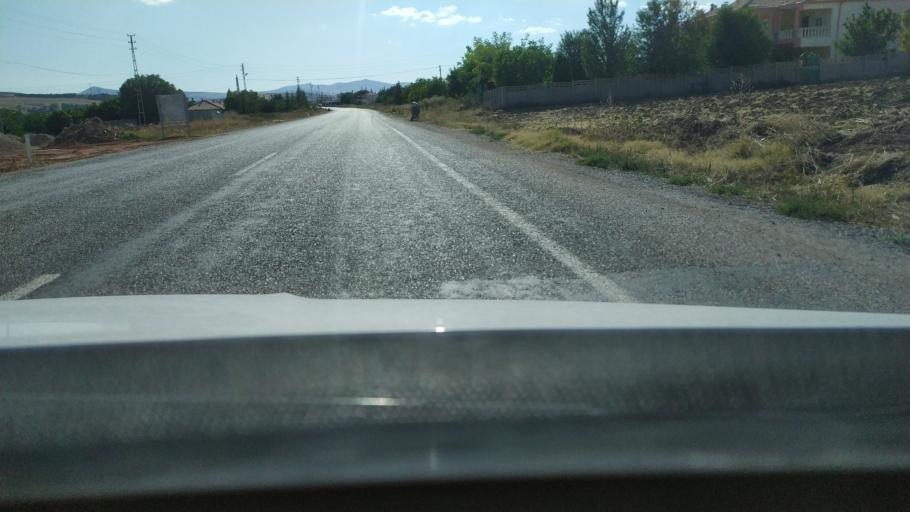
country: TR
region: Kayseri
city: Felahiye
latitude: 39.1024
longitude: 35.5905
